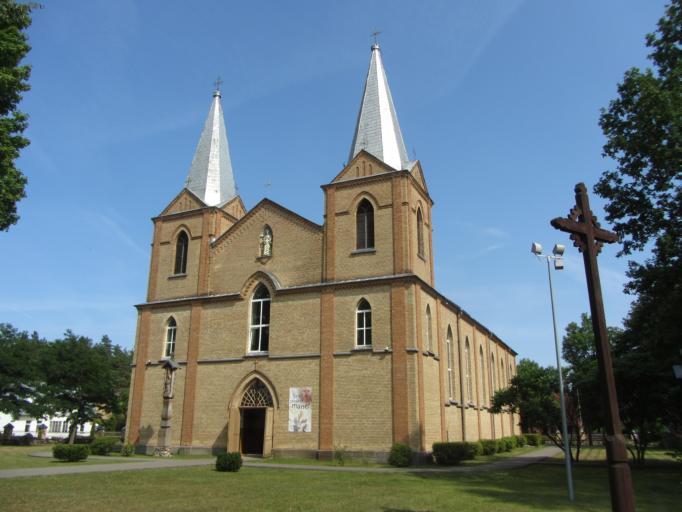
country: LT
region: Alytaus apskritis
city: Druskininkai
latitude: 54.0000
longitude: 24.0179
